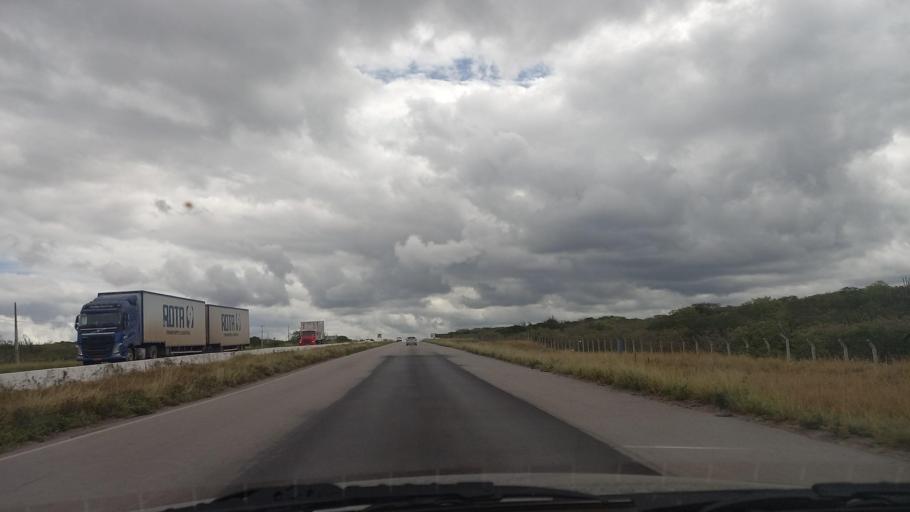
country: BR
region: Pernambuco
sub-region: Caruaru
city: Caruaru
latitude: -8.3200
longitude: -36.0722
